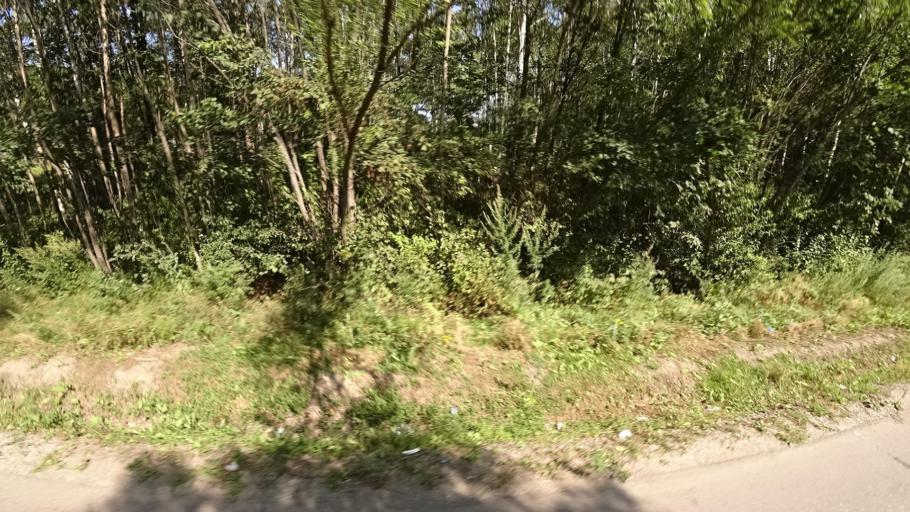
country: RU
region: Khabarovsk Krai
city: Khor
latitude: 47.9737
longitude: 135.1142
